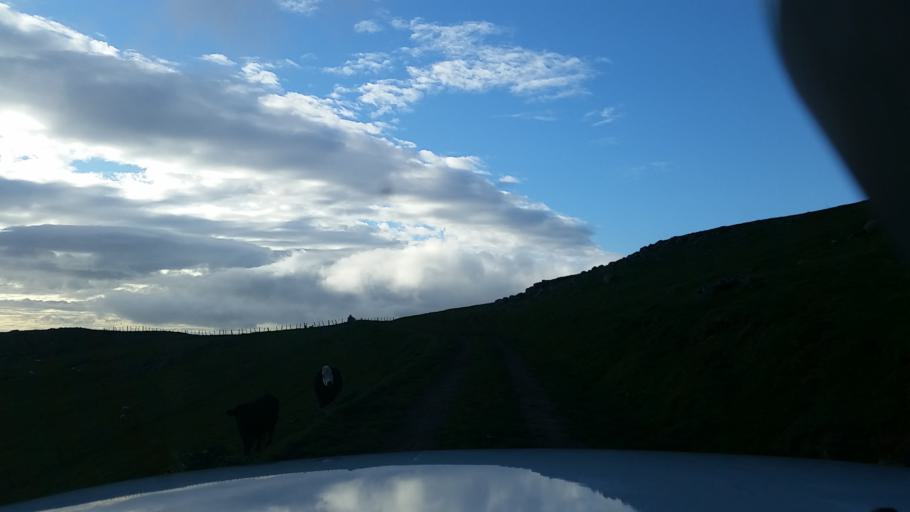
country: NZ
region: Canterbury
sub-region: Christchurch City
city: Christchurch
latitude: -43.6553
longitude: 172.8673
